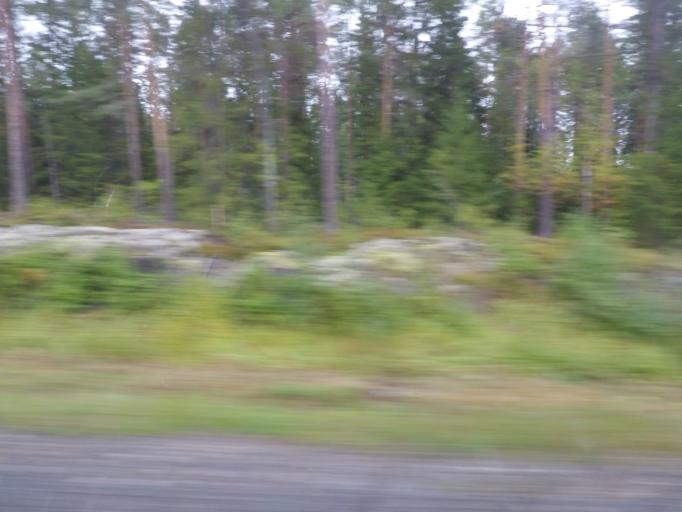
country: FI
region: Northern Savo
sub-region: Varkaus
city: Leppaevirta
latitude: 62.5249
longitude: 27.6683
